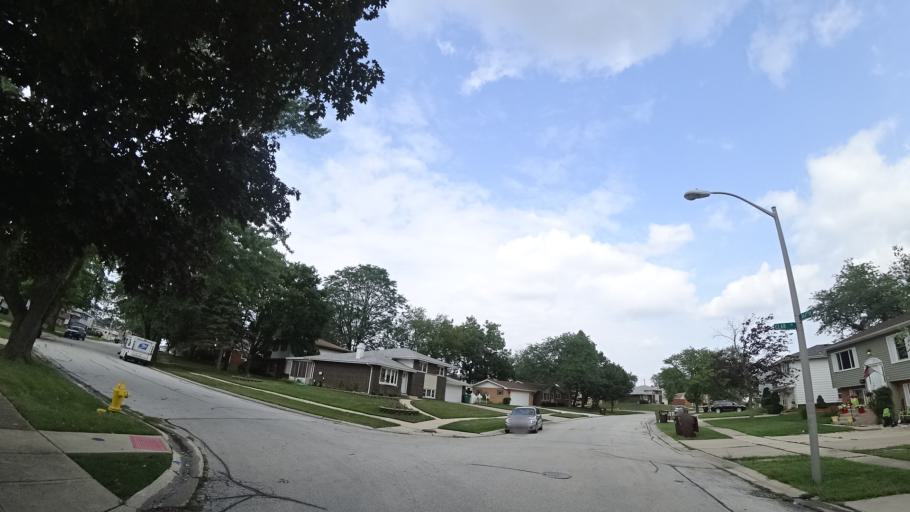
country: US
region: Illinois
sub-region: Cook County
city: Tinley Park
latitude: 41.5926
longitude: -87.7795
